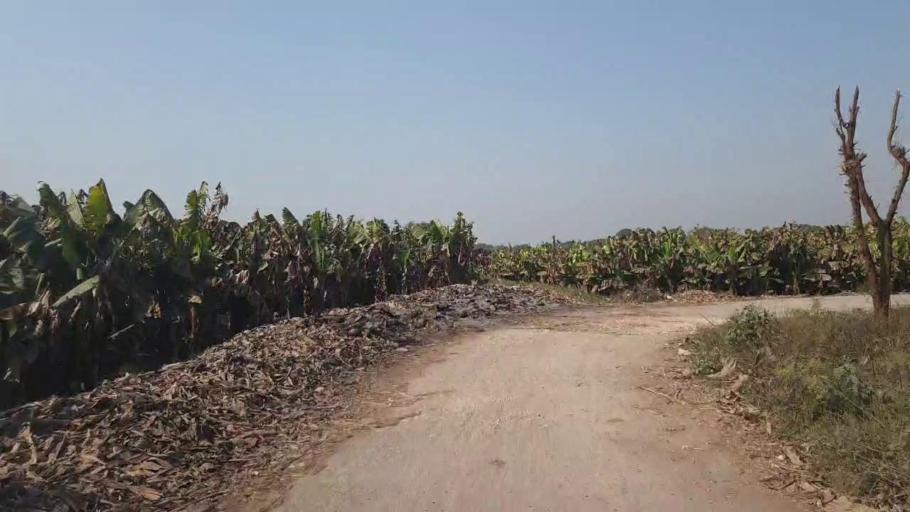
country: PK
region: Sindh
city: Tando Jam
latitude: 25.3292
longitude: 68.6010
